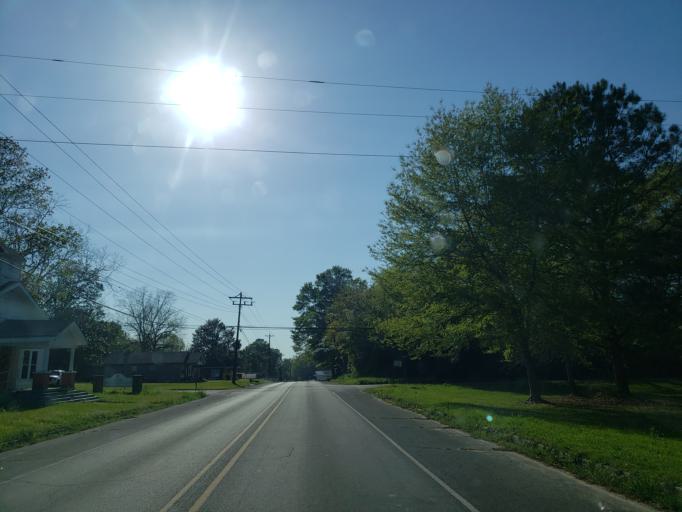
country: US
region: Mississippi
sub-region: Perry County
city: Richton
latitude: 31.4818
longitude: -89.0313
